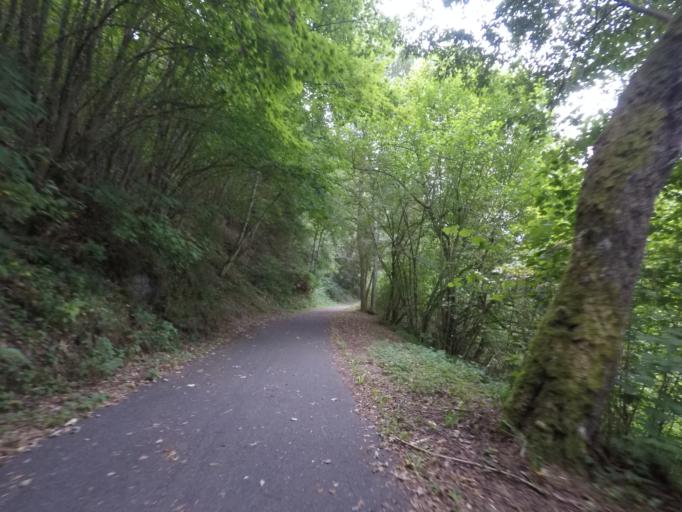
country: BE
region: Wallonia
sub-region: Province du Luxembourg
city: Martelange
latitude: 49.8419
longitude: 5.7271
